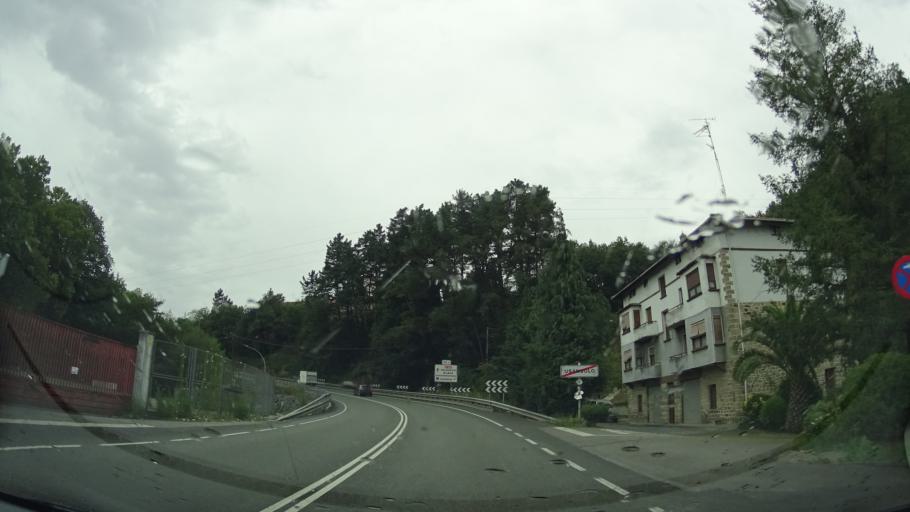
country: ES
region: Basque Country
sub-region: Bizkaia
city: Galdakao
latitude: 43.2216
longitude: -2.8162
